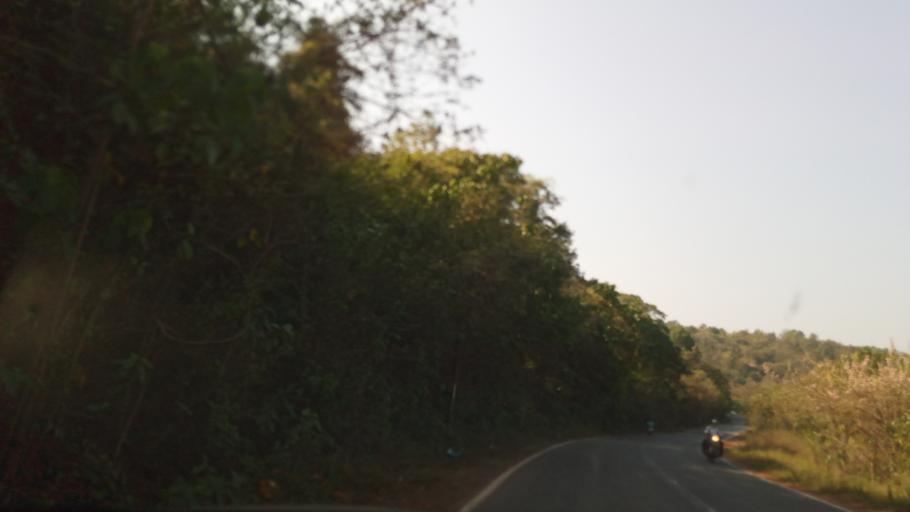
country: IN
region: Goa
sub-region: North Goa
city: Bandora
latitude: 15.4171
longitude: 73.9858
